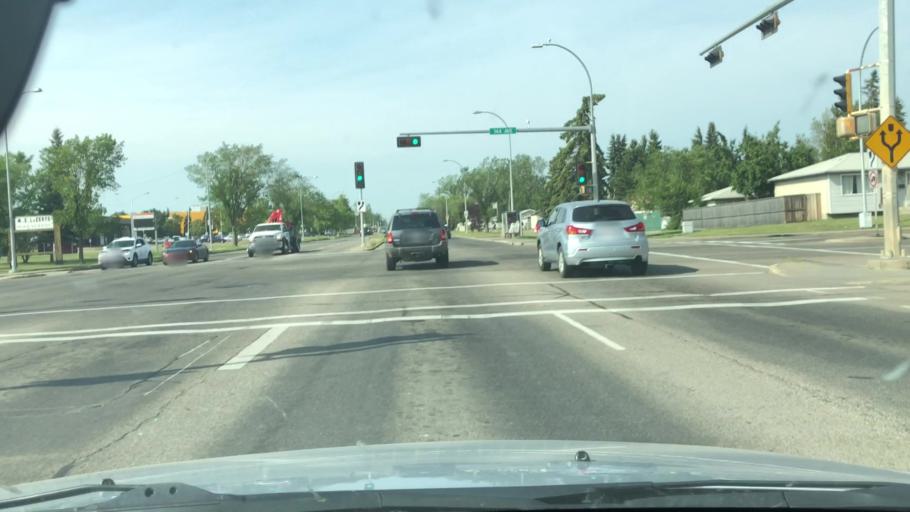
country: CA
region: Alberta
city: Edmonton
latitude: 53.6042
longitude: -113.4428
